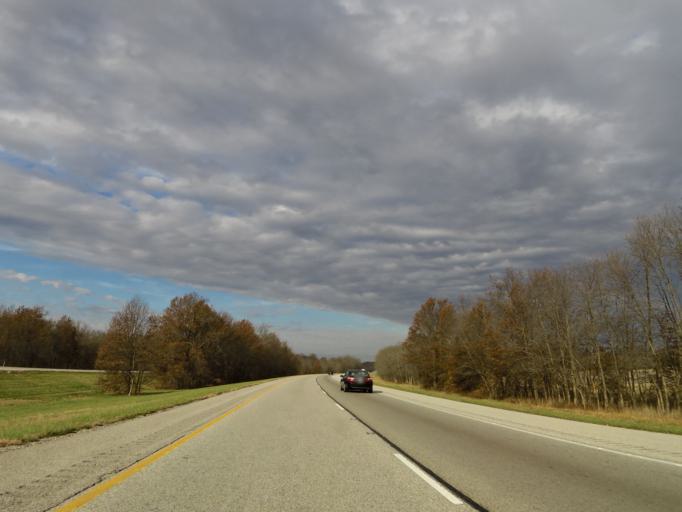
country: US
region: Illinois
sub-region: Washington County
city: Nashville
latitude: 38.3940
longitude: -89.3841
